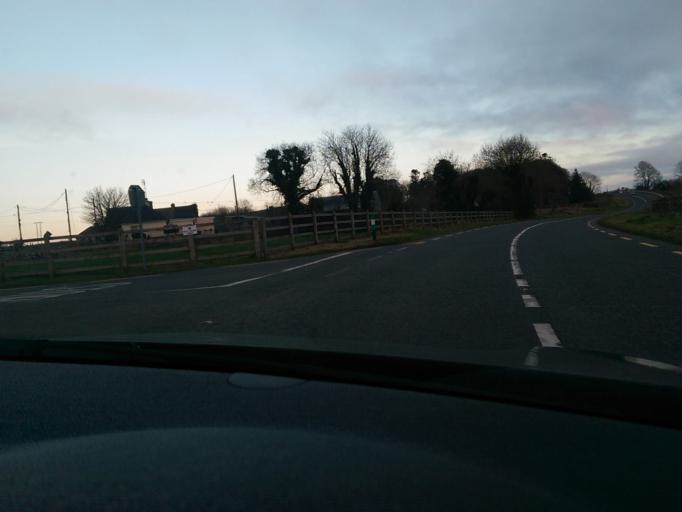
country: IE
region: Connaught
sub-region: Sligo
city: Ballymote
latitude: 53.9844
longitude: -8.4704
